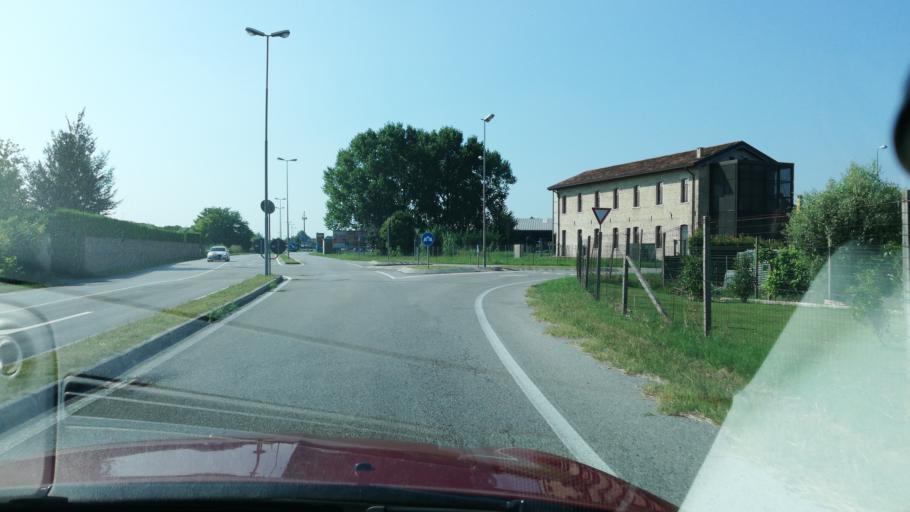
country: IT
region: Friuli Venezia Giulia
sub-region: Provincia di Udine
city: Latisana
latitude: 45.7790
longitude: 13.0026
